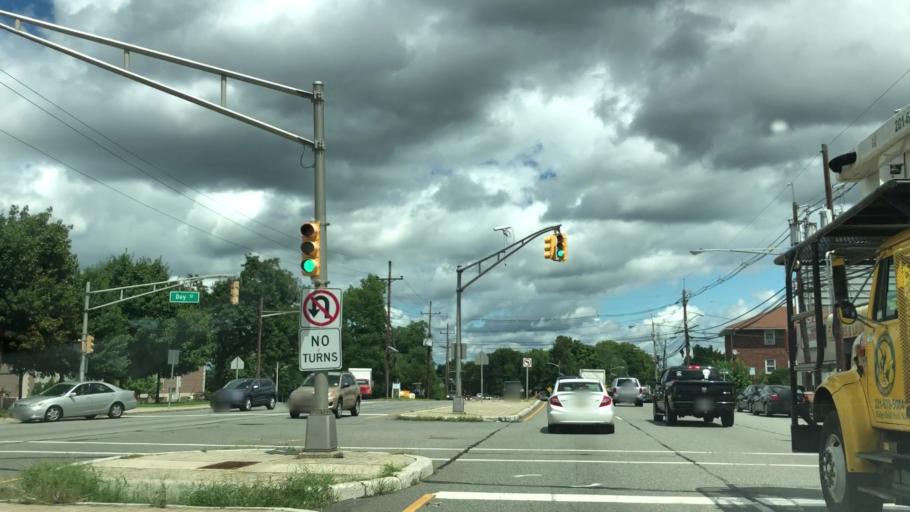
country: US
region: New Jersey
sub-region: Passaic County
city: Clifton
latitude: 40.8792
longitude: -74.1521
